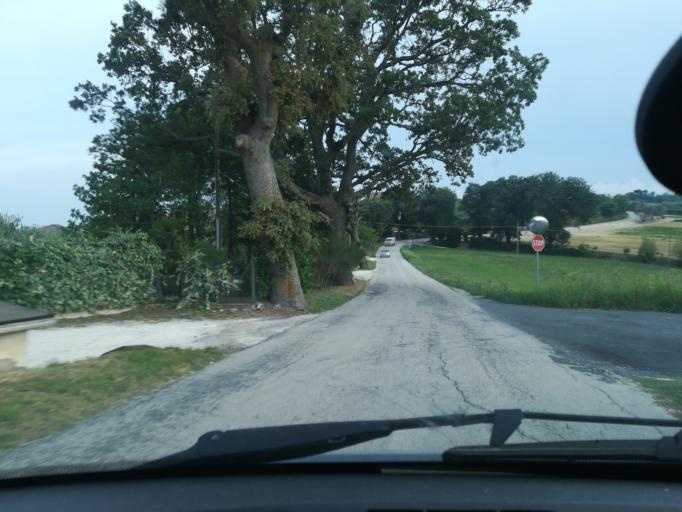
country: IT
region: The Marches
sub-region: Provincia di Macerata
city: Piediripa
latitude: 43.3026
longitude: 13.4790
